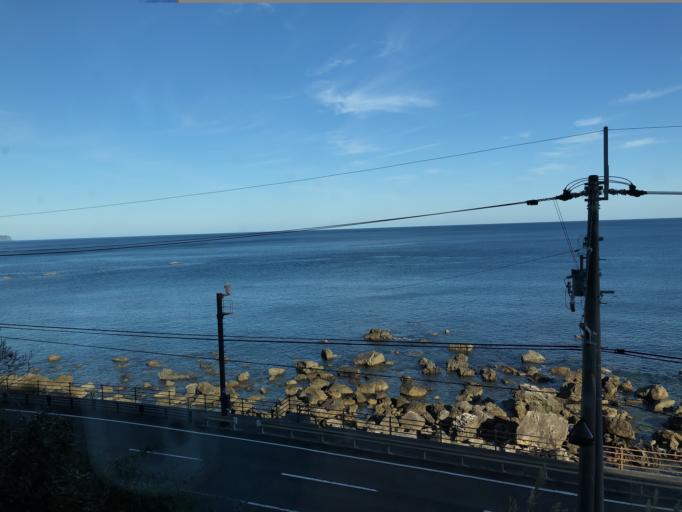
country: JP
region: Kochi
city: Nakamura
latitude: 33.0523
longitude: 133.0977
